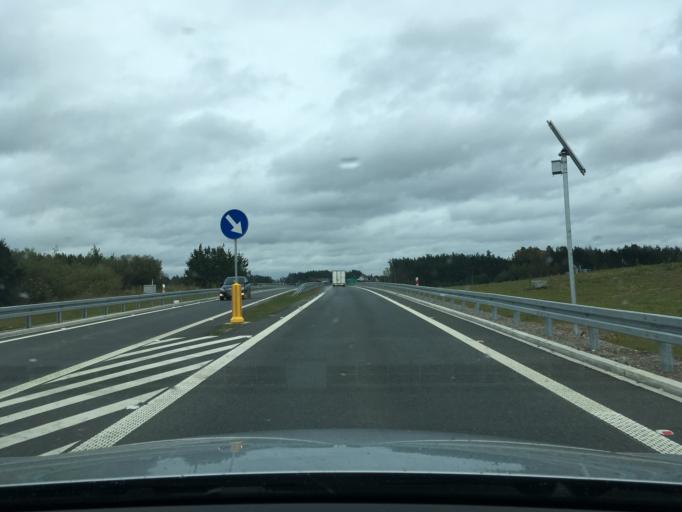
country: PL
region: Pomeranian Voivodeship
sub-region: Powiat koscierski
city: Koscierzyna
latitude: 54.1144
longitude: 18.0084
